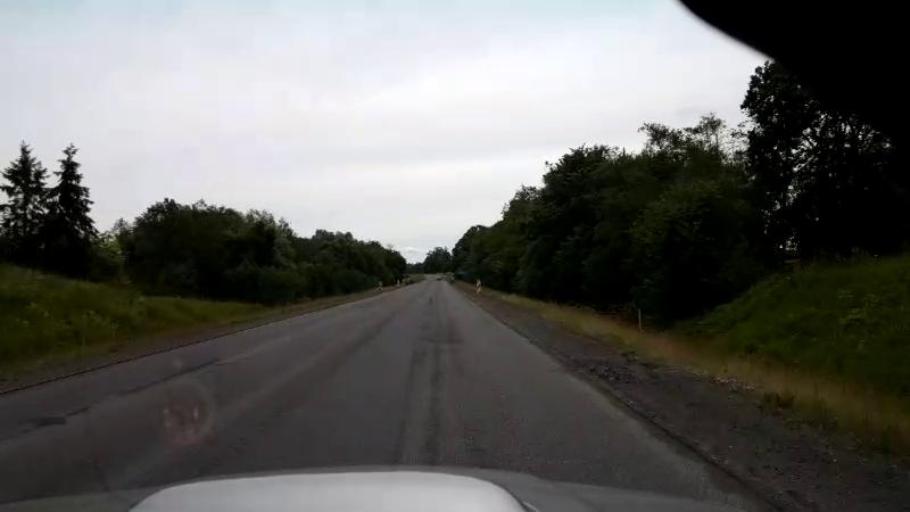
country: LV
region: Bauskas Rajons
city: Bauska
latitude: 56.3258
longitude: 24.3090
